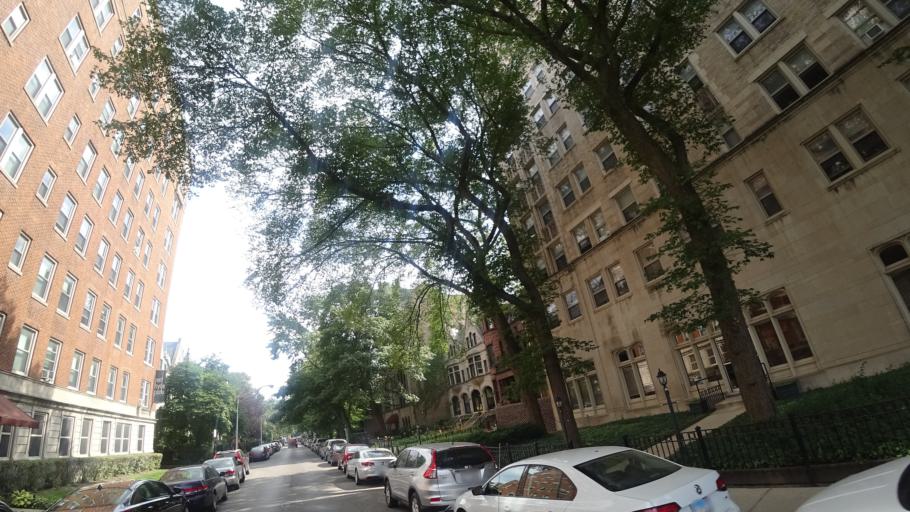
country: US
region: Illinois
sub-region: Cook County
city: Chicago
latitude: 41.8023
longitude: -87.5918
